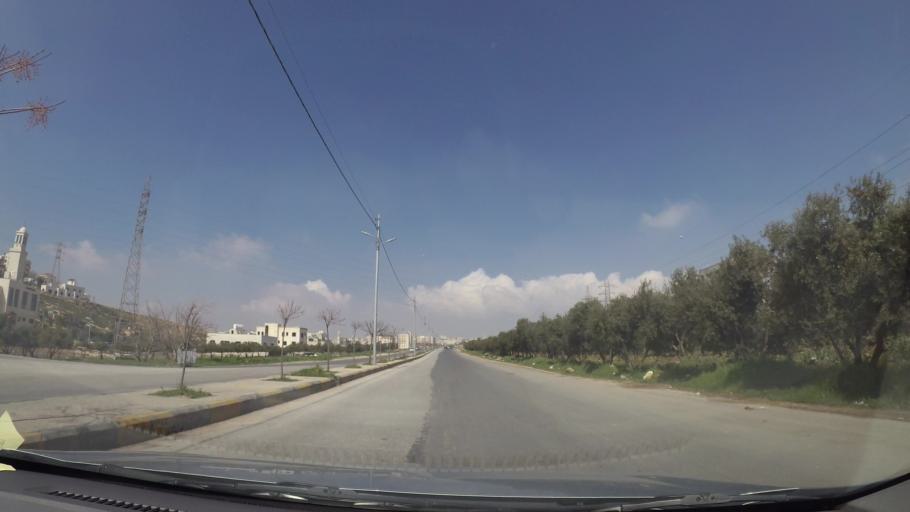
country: JO
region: Amman
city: Al Bunayyat ash Shamaliyah
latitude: 31.8914
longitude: 35.9032
